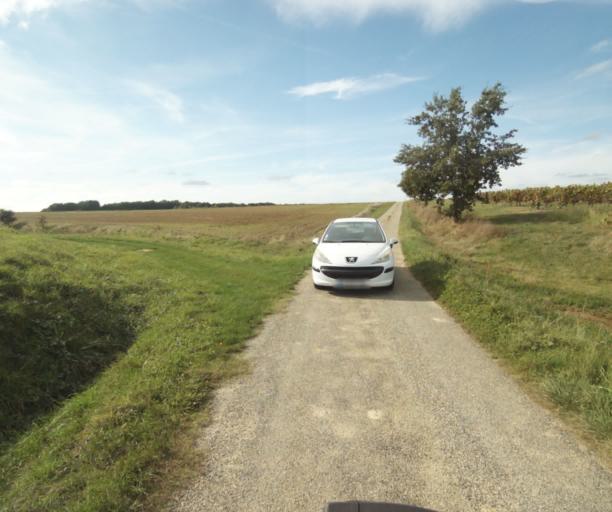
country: FR
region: Midi-Pyrenees
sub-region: Departement du Tarn-et-Garonne
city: Saint-Porquier
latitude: 43.9493
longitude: 1.1433
